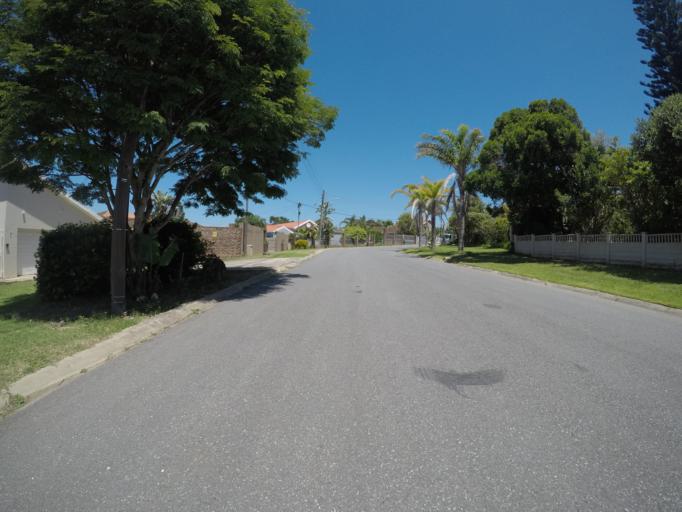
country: ZA
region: Eastern Cape
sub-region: Buffalo City Metropolitan Municipality
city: East London
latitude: -32.9666
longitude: 27.9542
